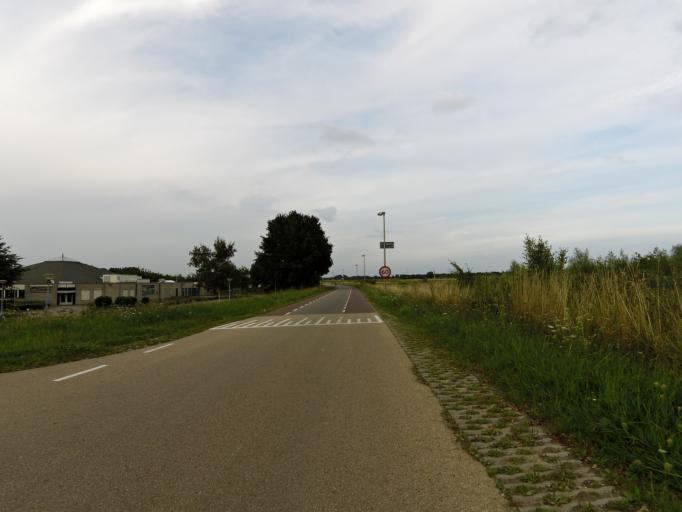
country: NL
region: Gelderland
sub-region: Gemeente Doesburg
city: Doesburg
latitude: 52.0062
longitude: 6.1544
